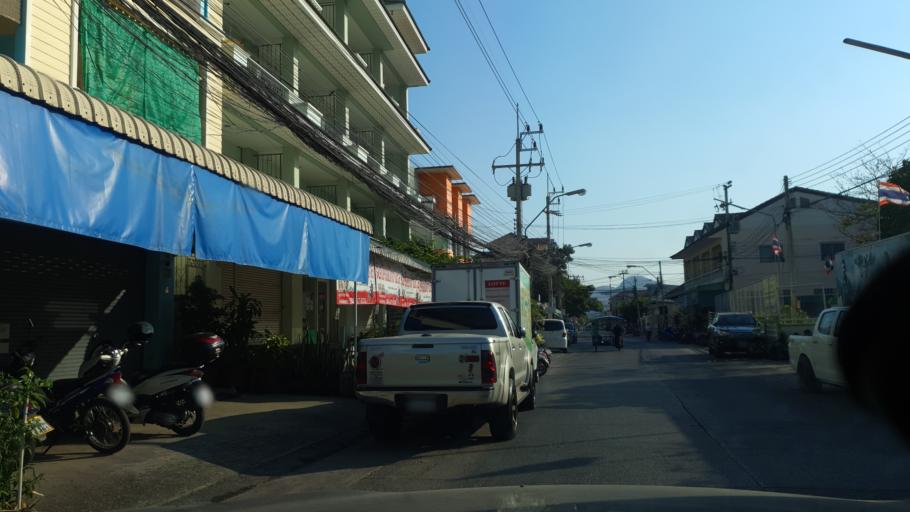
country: TH
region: Prachuap Khiri Khan
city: Hua Hin
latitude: 12.5572
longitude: 99.9527
